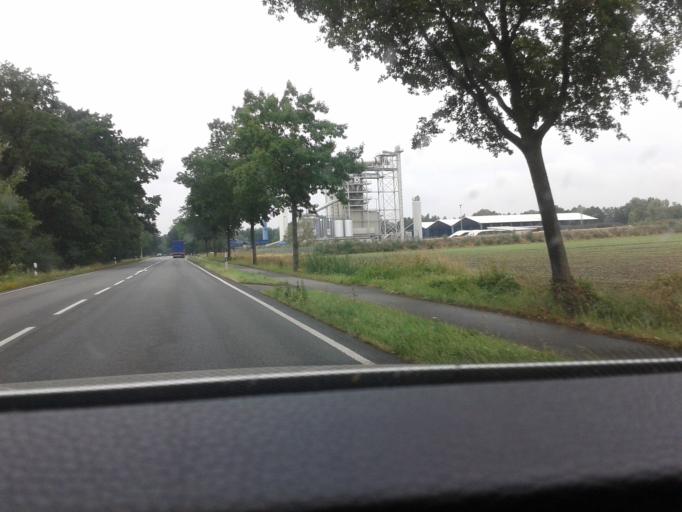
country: DE
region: Lower Saxony
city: Osloss
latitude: 52.4753
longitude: 10.6597
